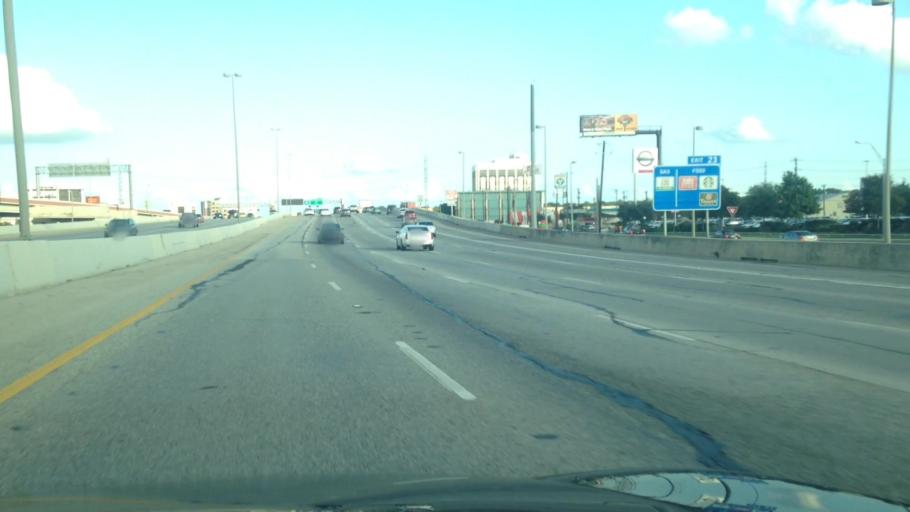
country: US
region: Texas
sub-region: Bexar County
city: Alamo Heights
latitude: 29.5178
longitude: -98.4676
